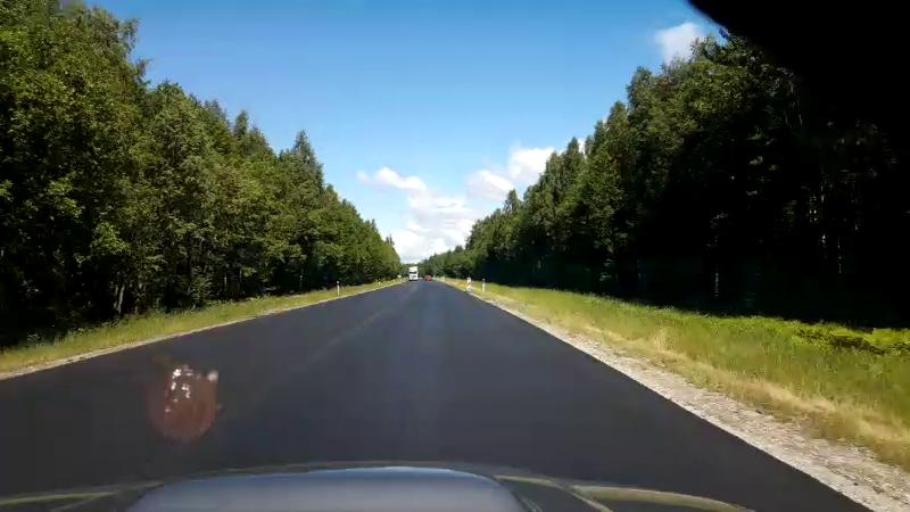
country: LV
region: Salacgrivas
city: Ainazi
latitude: 58.0220
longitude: 24.4999
